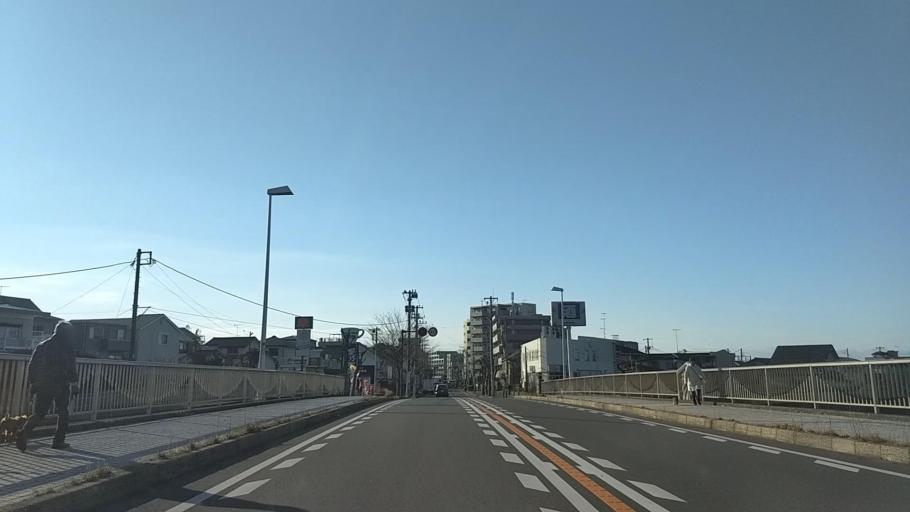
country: JP
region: Kanagawa
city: Fujisawa
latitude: 35.3226
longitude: 139.4864
